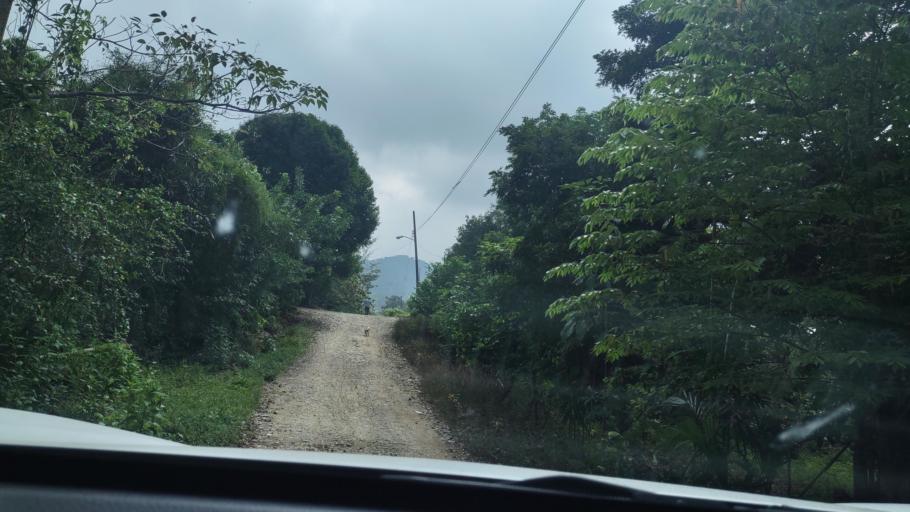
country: MX
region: Veracruz
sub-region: Uxpanapa
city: Poblado 10
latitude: 17.5196
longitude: -94.3036
